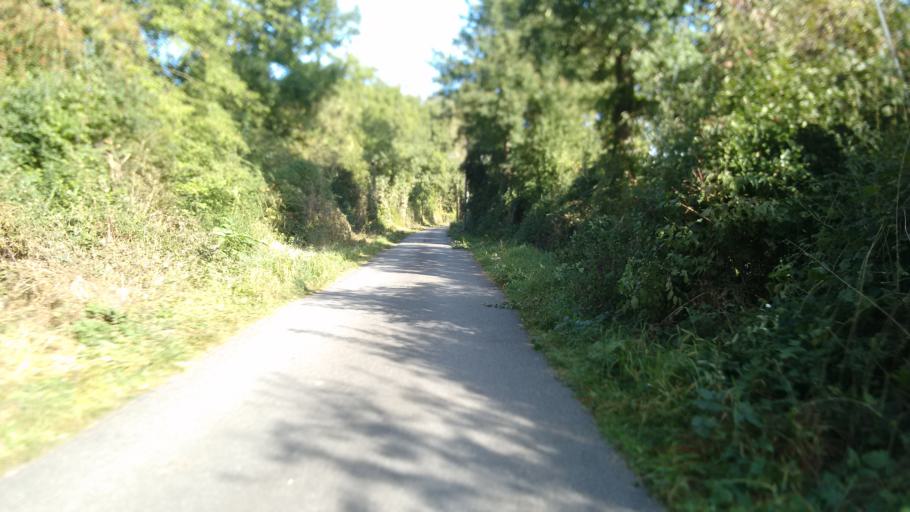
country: DE
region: Rheinland-Pfalz
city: Nieder-Ingelheim
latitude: 49.9969
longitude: 8.0650
